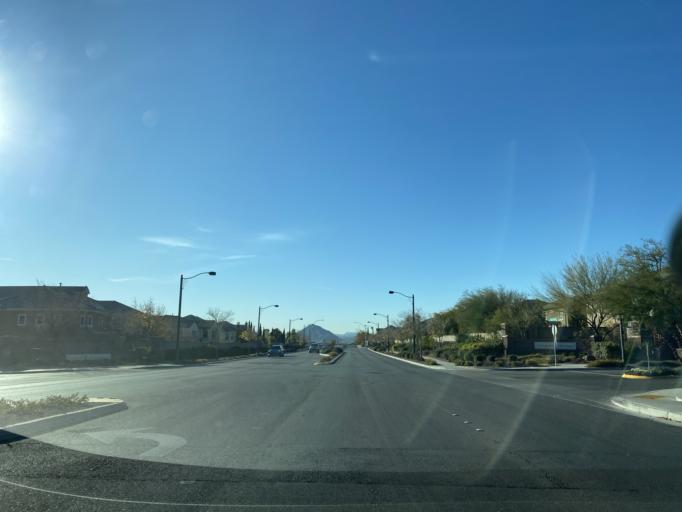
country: US
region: Nevada
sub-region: Clark County
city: Summerlin South
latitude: 36.2904
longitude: -115.3196
